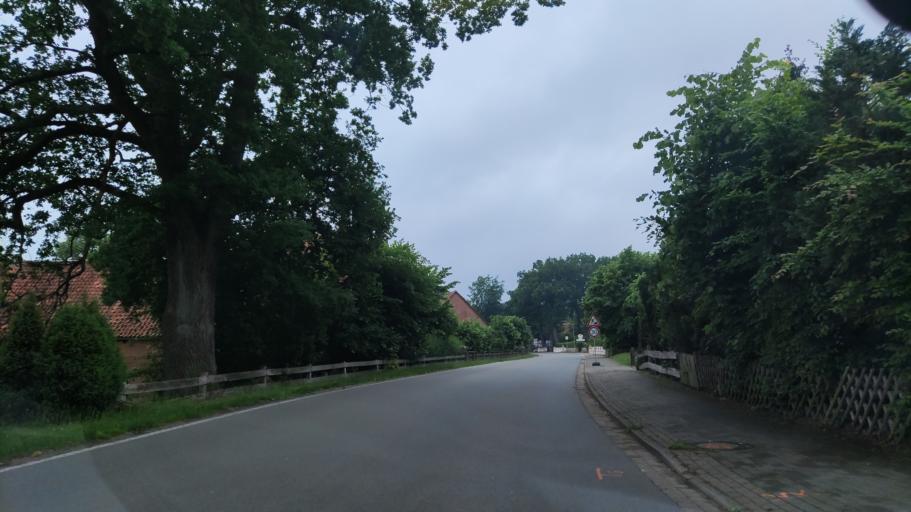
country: DE
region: Lower Saxony
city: Wriedel
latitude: 53.0181
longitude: 10.2835
